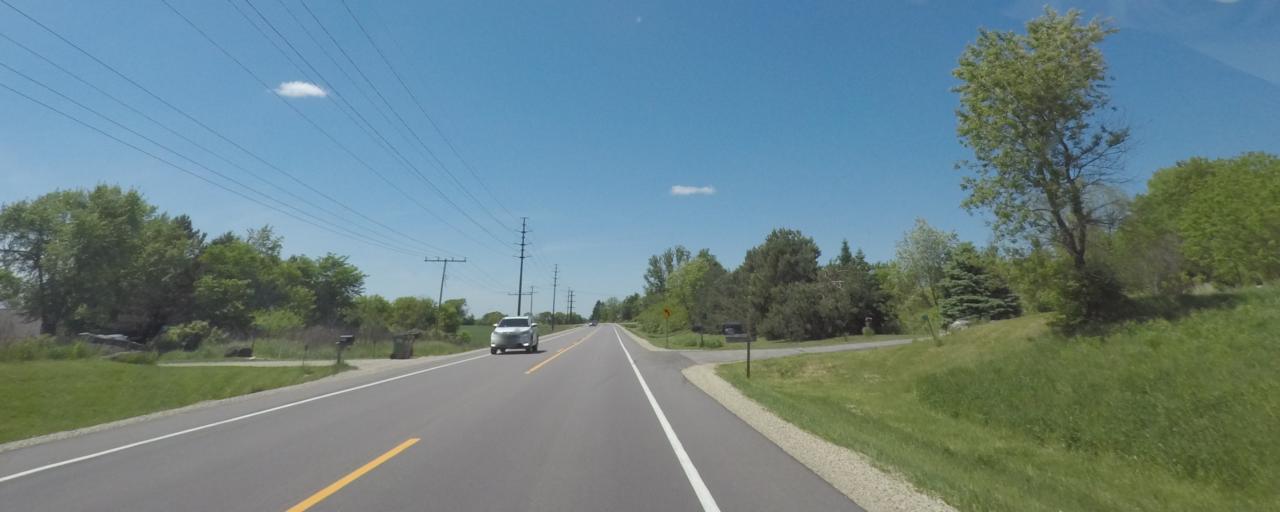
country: US
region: Wisconsin
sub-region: Dane County
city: Fitchburg
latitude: 42.9697
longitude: -89.4977
